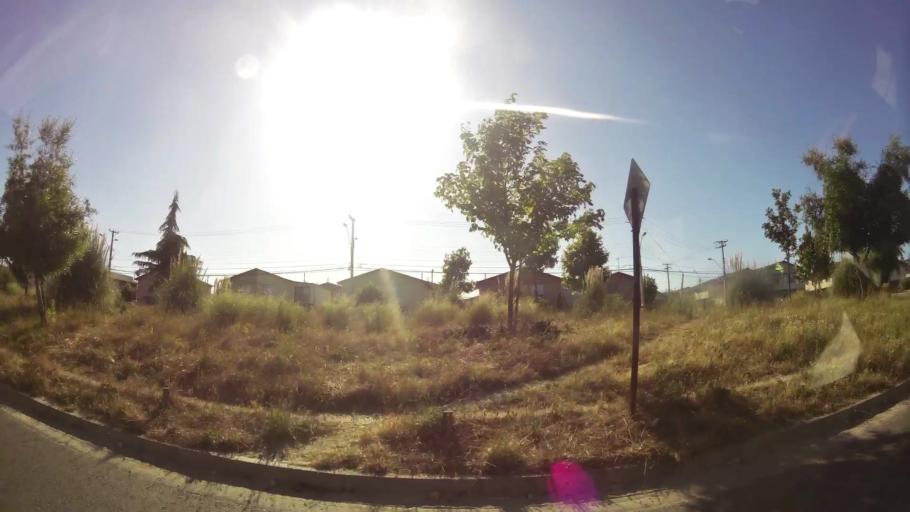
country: CL
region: Valparaiso
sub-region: Provincia de Valparaiso
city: Valparaiso
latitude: -33.1189
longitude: -71.5795
